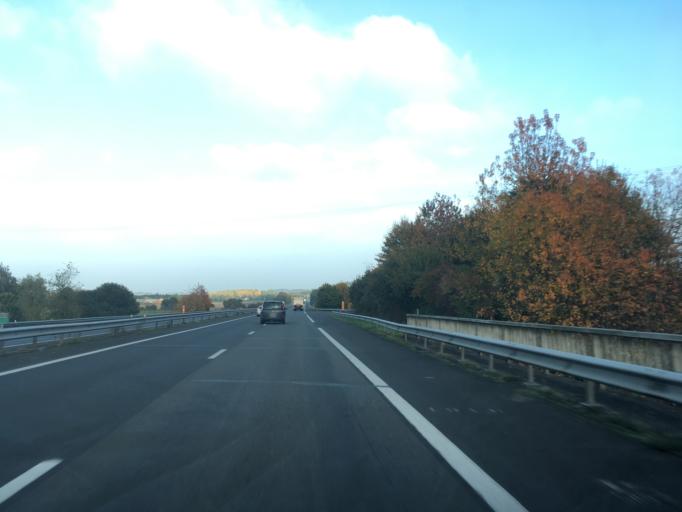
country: FR
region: Pays de la Loire
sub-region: Departement de la Sarthe
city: Louplande
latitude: 47.9464
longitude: -0.0203
